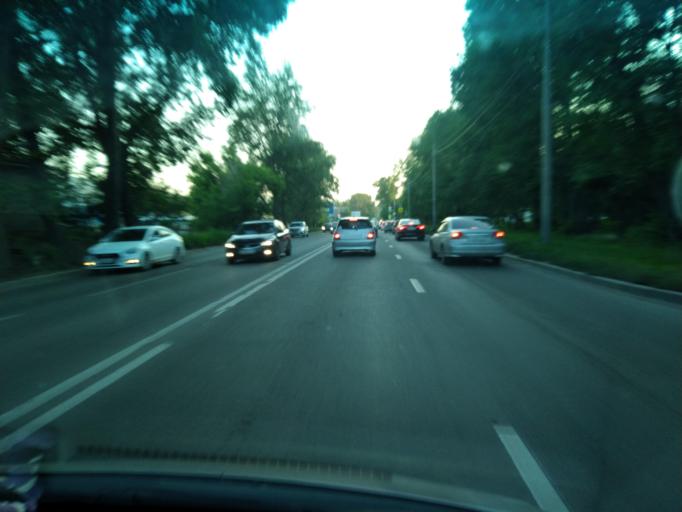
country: RU
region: Krasnoyarskiy
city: Krasnoyarsk
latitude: 55.9874
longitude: 92.9002
